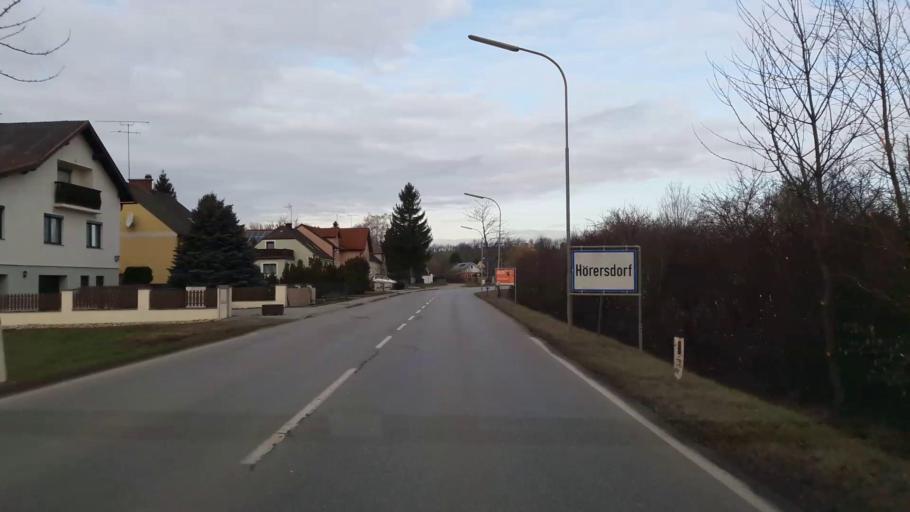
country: AT
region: Lower Austria
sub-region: Politischer Bezirk Mistelbach
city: Asparn an der Zaya
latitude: 48.6206
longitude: 16.5184
